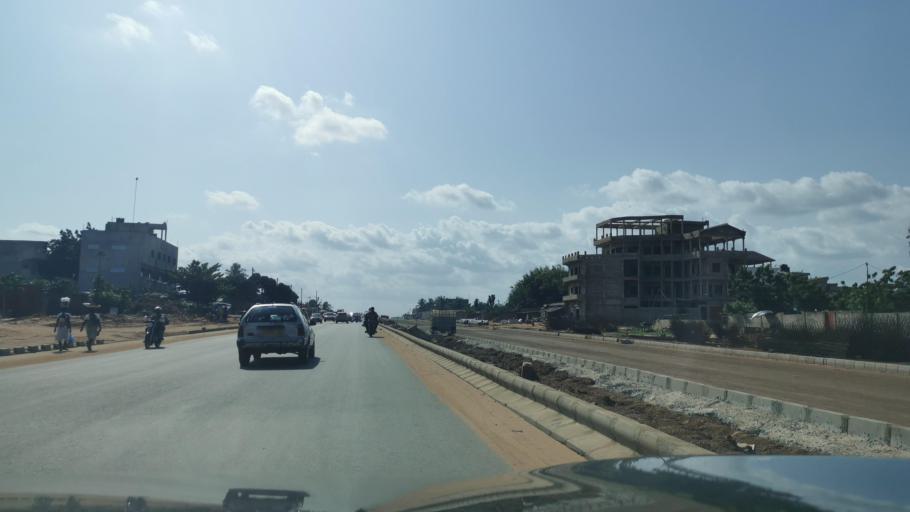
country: TG
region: Maritime
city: Lome
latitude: 6.2158
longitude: 1.1307
